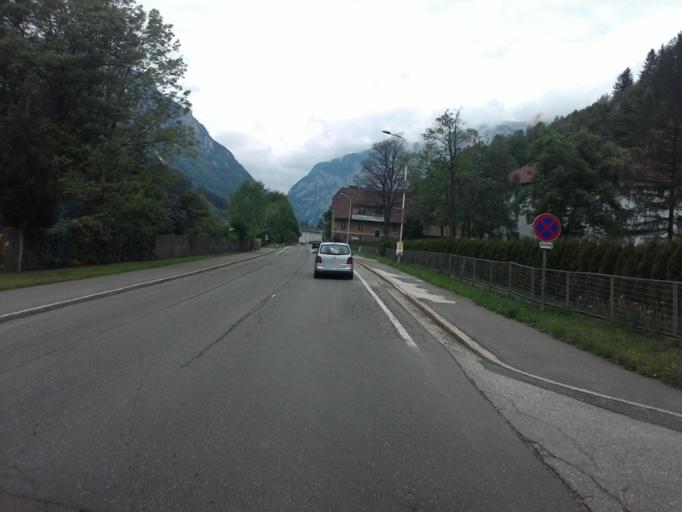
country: AT
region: Styria
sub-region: Politischer Bezirk Leoben
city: Eisenerz
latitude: 47.5460
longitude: 14.8824
